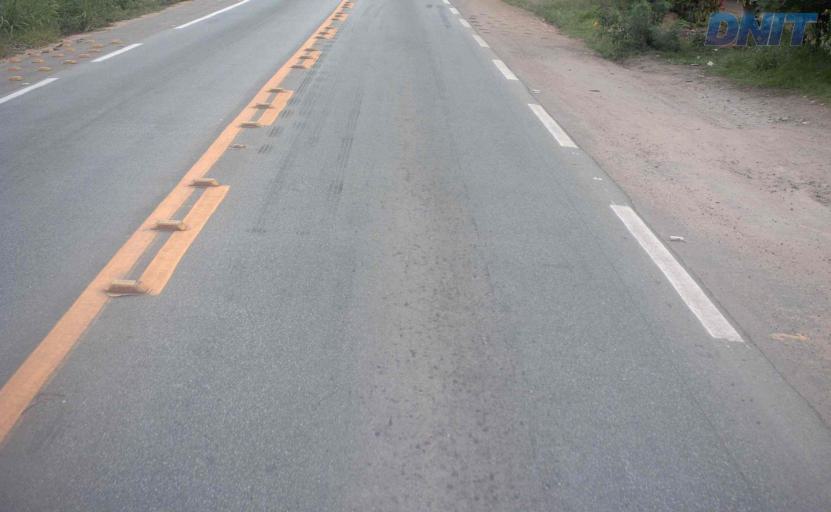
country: BR
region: Minas Gerais
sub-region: Timoteo
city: Timoteo
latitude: -19.5605
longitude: -42.7104
